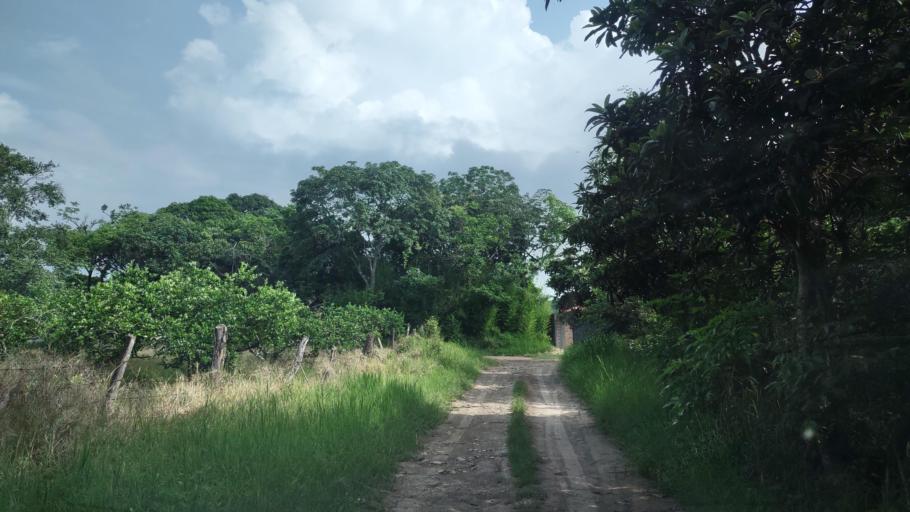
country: MX
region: Veracruz
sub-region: Coatepec
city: Bella Esperanza
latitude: 19.4466
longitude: -96.8272
